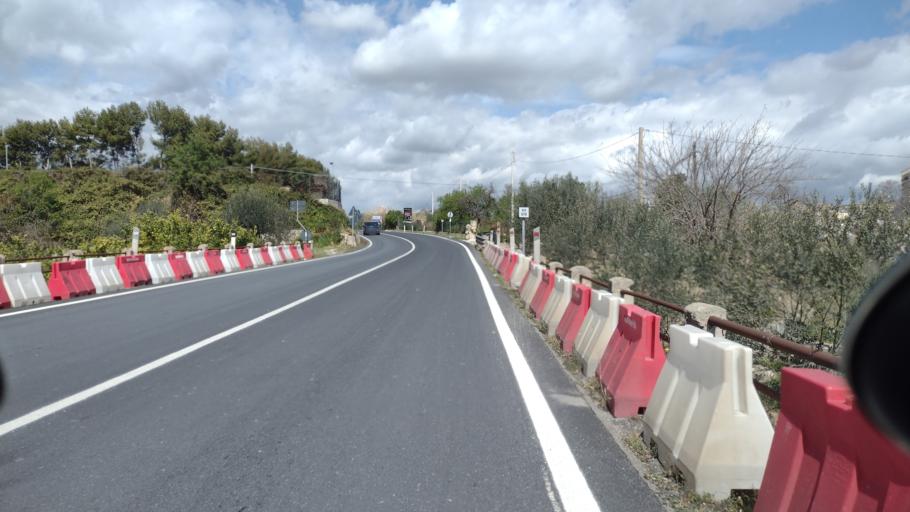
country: IT
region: Sicily
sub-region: Provincia di Siracusa
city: Noto
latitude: 36.8832
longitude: 15.0631
